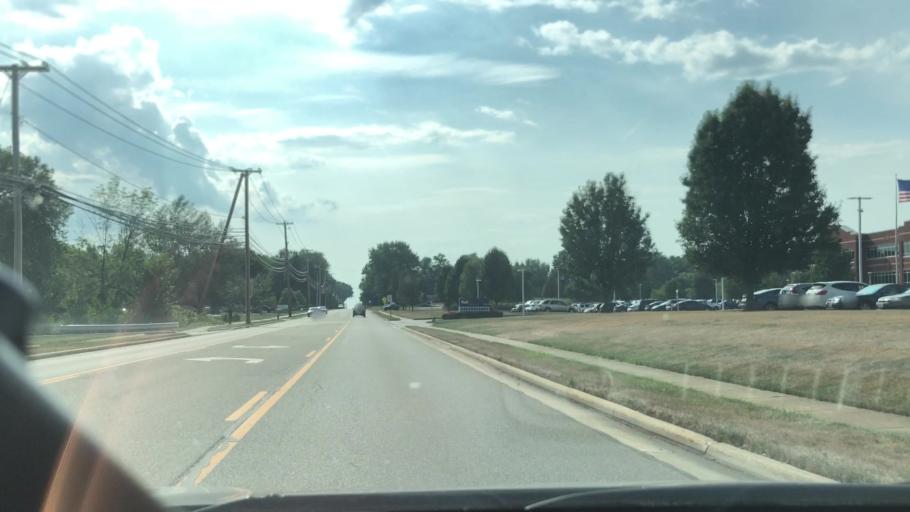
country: US
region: Ohio
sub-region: Summit County
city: Green
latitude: 40.9595
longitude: -81.4742
